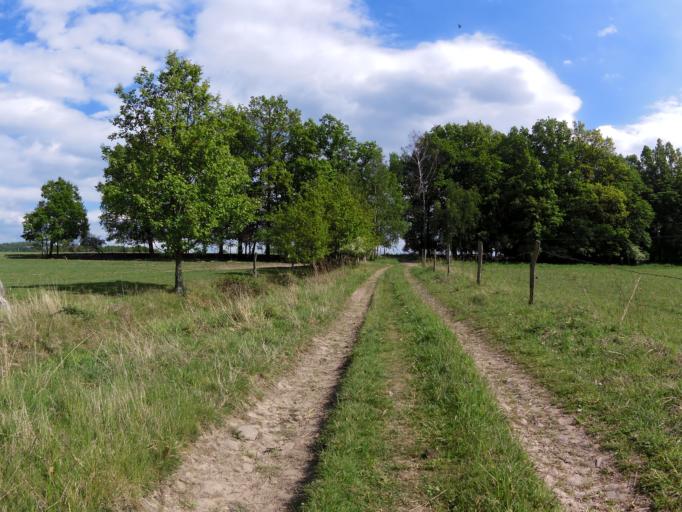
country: DE
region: Thuringia
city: Seebach
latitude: 50.9580
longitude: 10.4280
